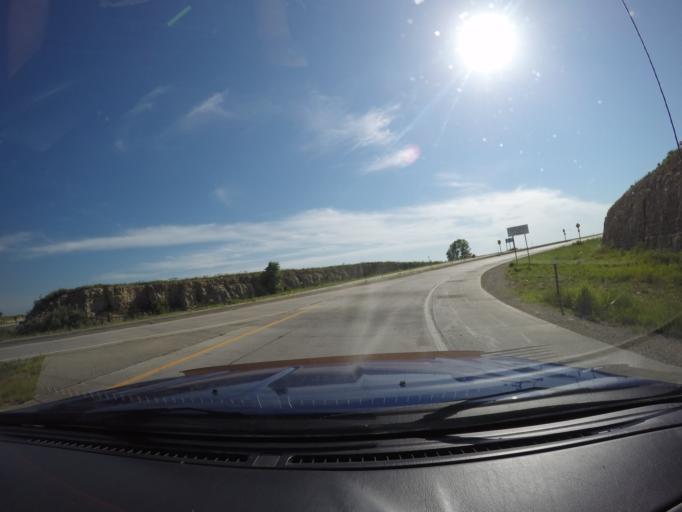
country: US
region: Kansas
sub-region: Riley County
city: Manhattan
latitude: 39.0615
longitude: -96.5387
